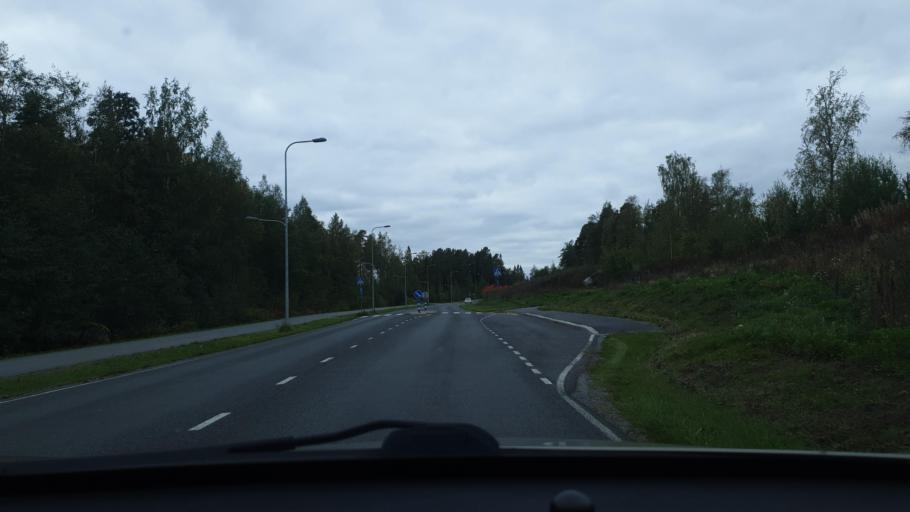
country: FI
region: Ostrobothnia
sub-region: Vaasa
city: Teeriniemi
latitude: 63.1019
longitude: 21.6854
